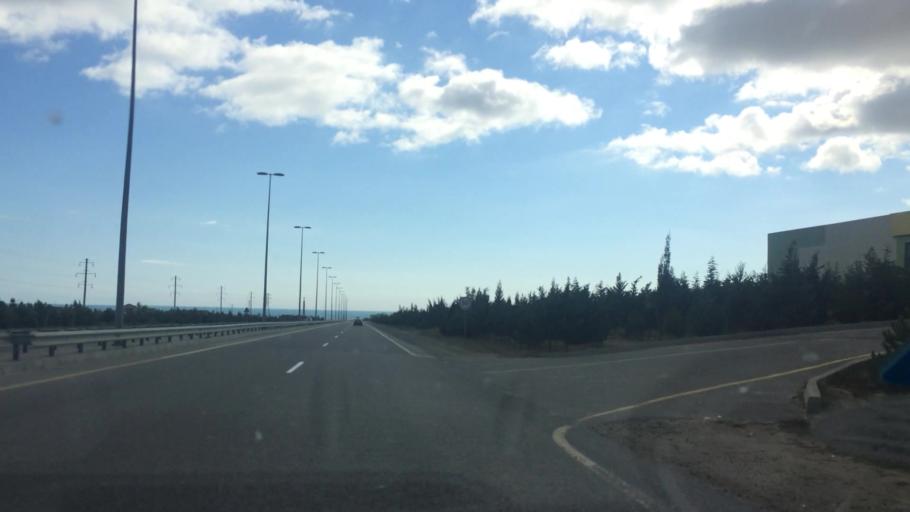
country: AZ
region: Baki
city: Zyrya
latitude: 40.4040
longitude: 50.3043
